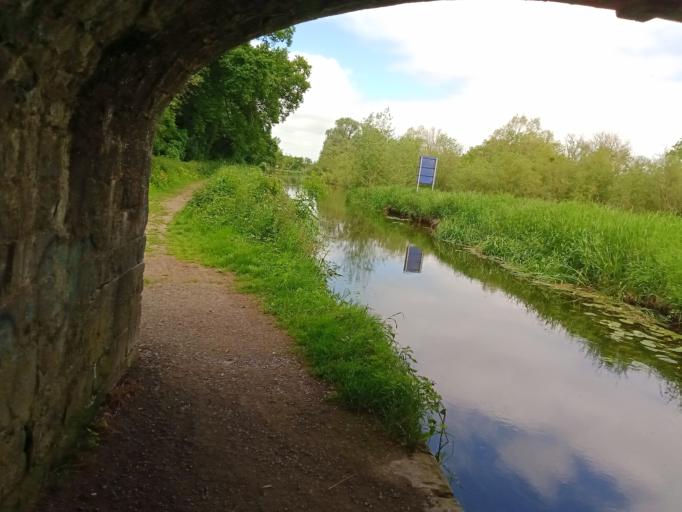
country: IE
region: Leinster
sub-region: County Carlow
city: Carlow
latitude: 52.7817
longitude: -6.9660
